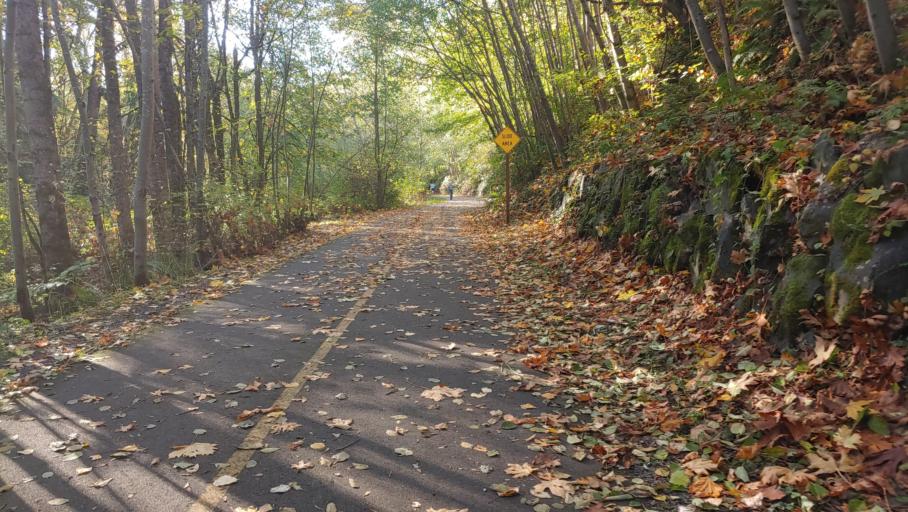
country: US
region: Washington
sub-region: King County
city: Des Moines
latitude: 47.4116
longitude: -122.3224
